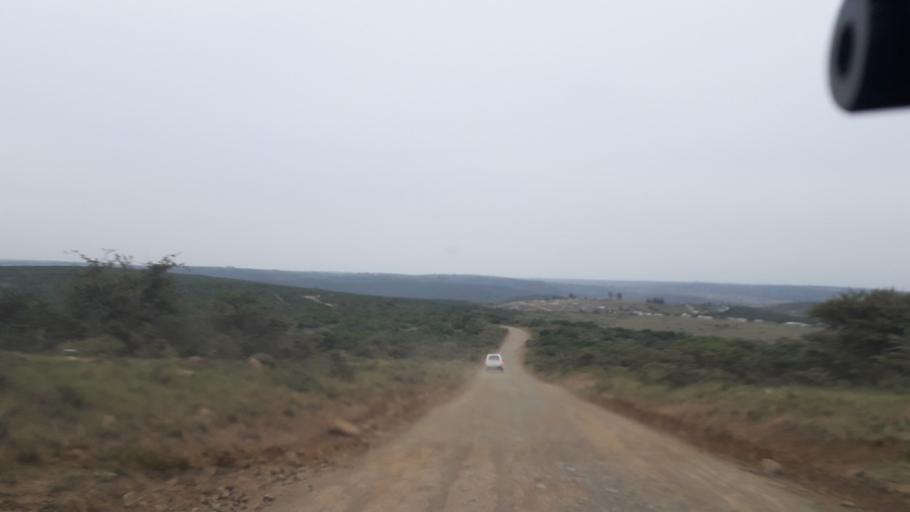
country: ZA
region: Eastern Cape
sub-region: Buffalo City Metropolitan Municipality
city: Bhisho
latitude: -32.7904
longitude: 27.3275
